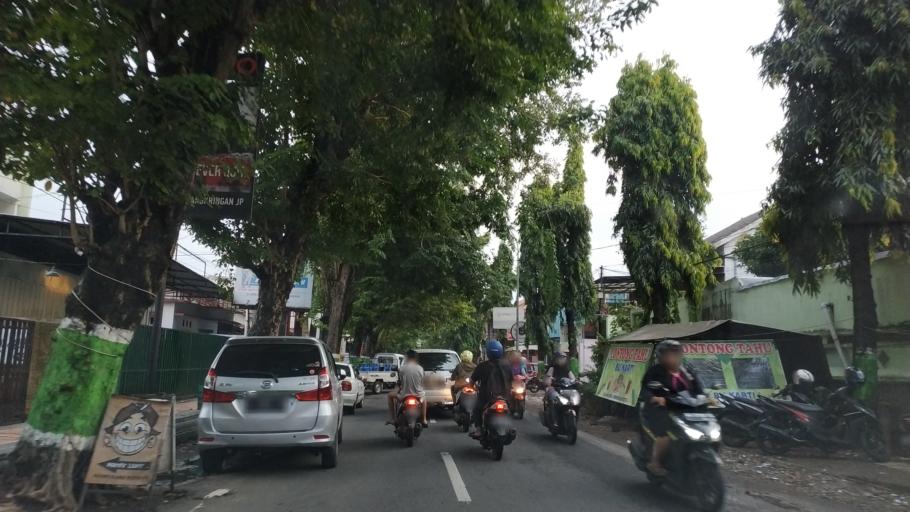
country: ID
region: Central Java
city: Kudus
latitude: -6.8069
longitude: 110.8559
